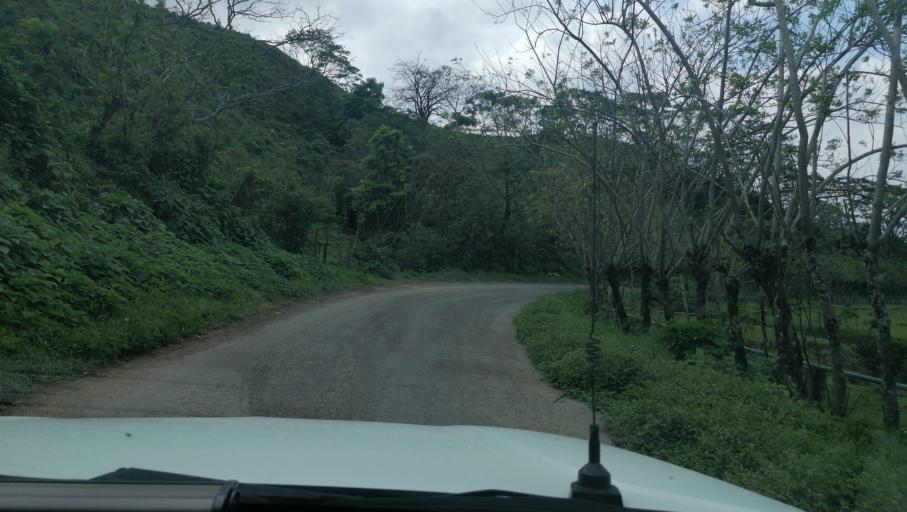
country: MX
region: Chiapas
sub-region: Francisco Leon
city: San Miguel la Sardina
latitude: 17.2383
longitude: -93.3037
